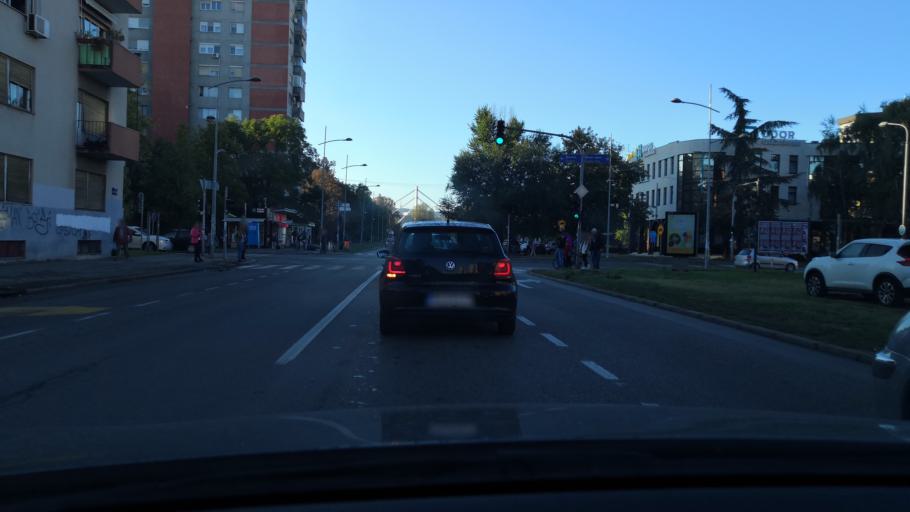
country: RS
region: Autonomna Pokrajina Vojvodina
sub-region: Juznobacki Okrug
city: Novi Sad
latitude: 45.2429
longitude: 19.8475
